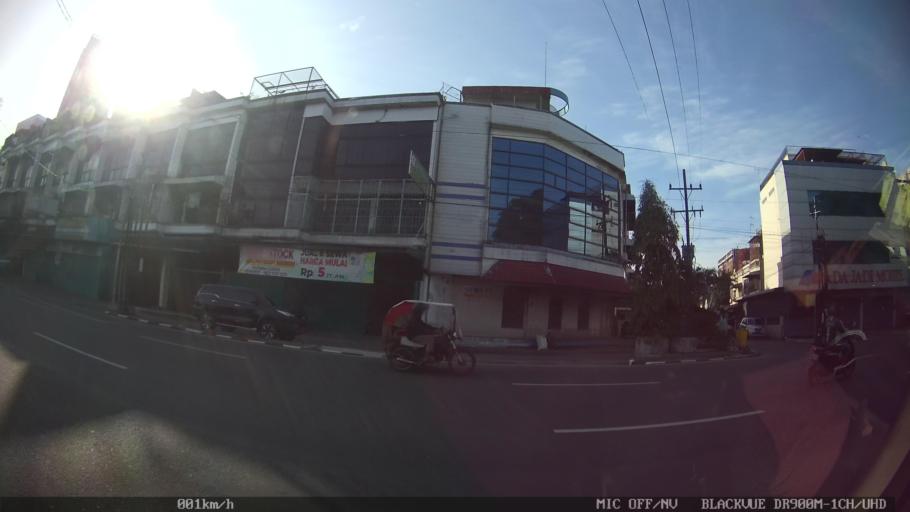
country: ID
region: North Sumatra
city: Medan
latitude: 3.5940
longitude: 98.6712
